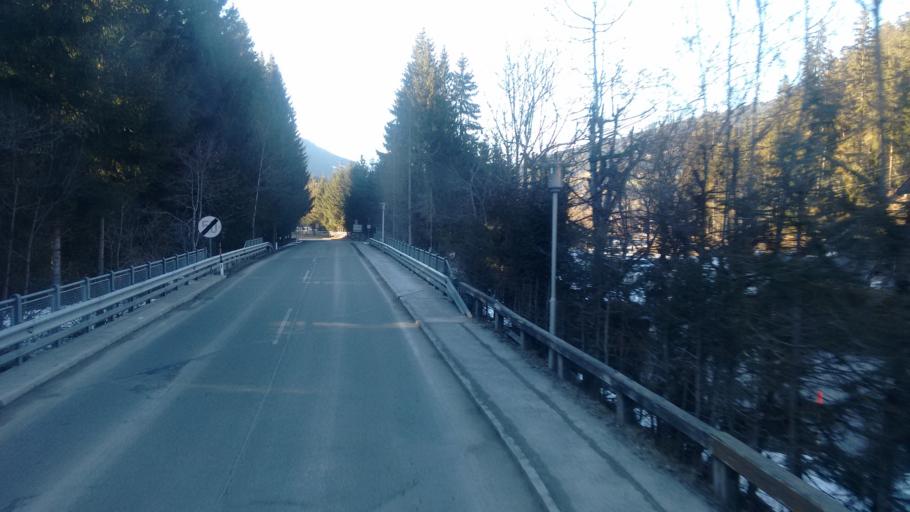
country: AT
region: Salzburg
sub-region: Politischer Bezirk Sankt Johann im Pongau
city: Altenmarkt im Pongau
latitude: 47.3641
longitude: 13.4252
